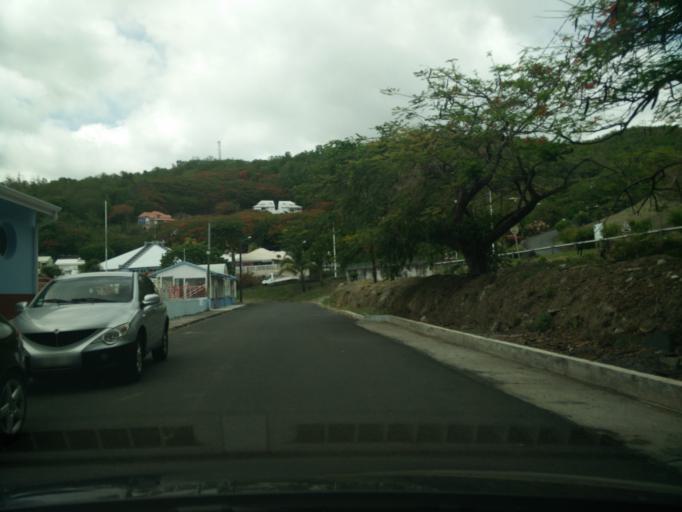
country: GP
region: Guadeloupe
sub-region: Guadeloupe
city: Basse-Terre
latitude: 15.9819
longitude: -61.7154
